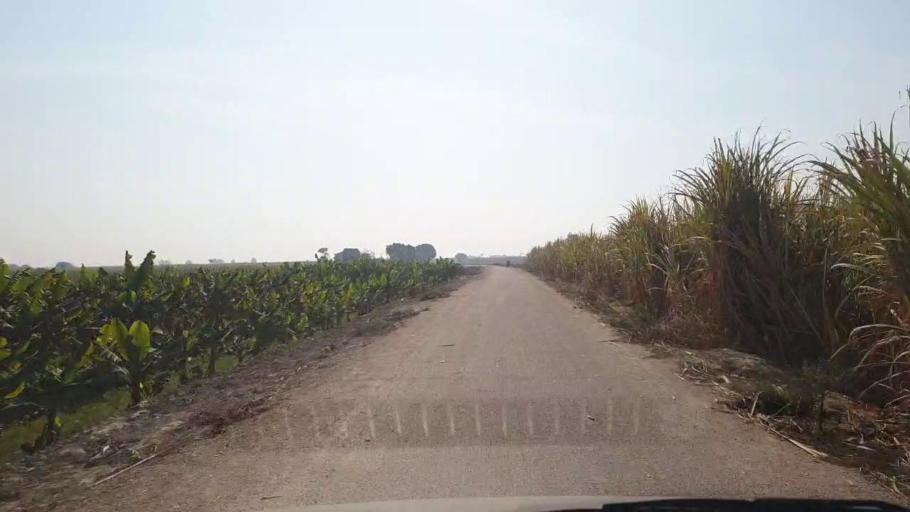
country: PK
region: Sindh
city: Tando Allahyar
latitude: 25.4031
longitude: 68.7400
